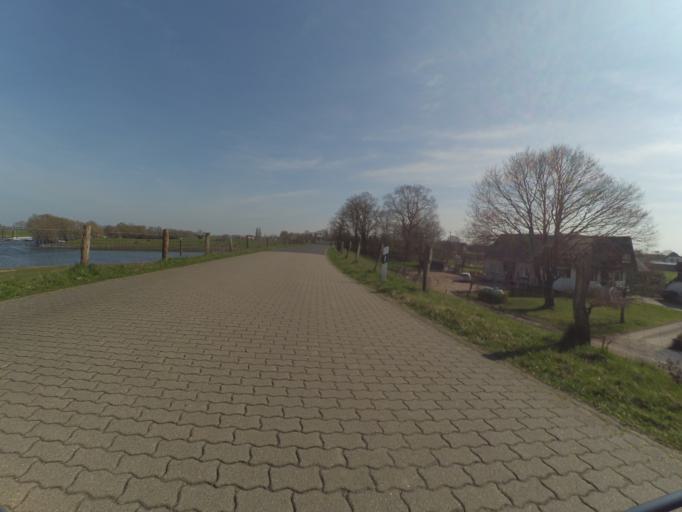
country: DE
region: North Rhine-Westphalia
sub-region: Regierungsbezirk Dusseldorf
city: Kleve
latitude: 51.8282
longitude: 6.1361
